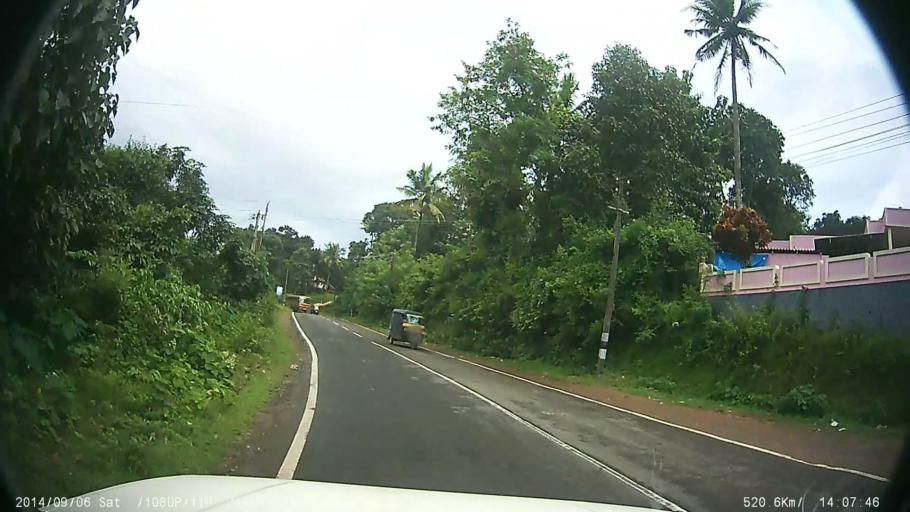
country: IN
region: Kerala
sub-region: Kottayam
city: Palackattumala
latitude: 9.6993
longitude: 76.5561
